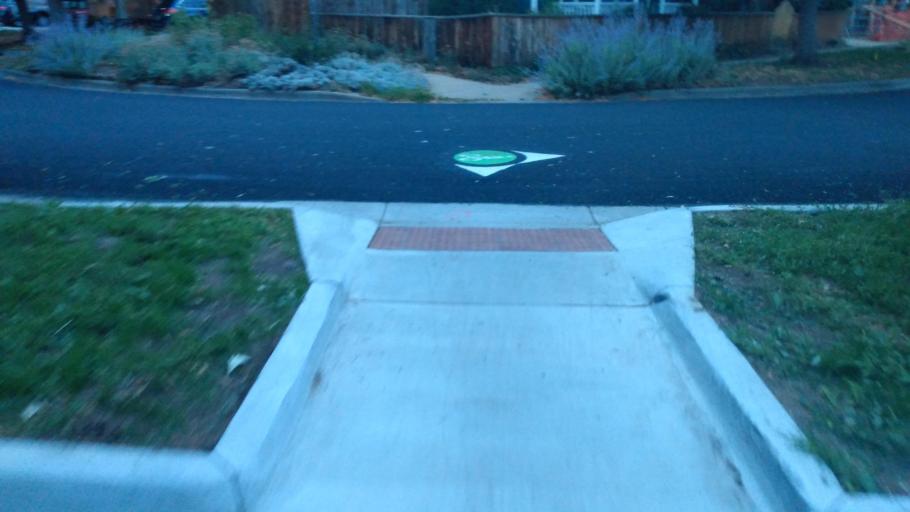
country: US
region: Colorado
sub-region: Boulder County
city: Boulder
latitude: 40.0162
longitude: -105.2647
